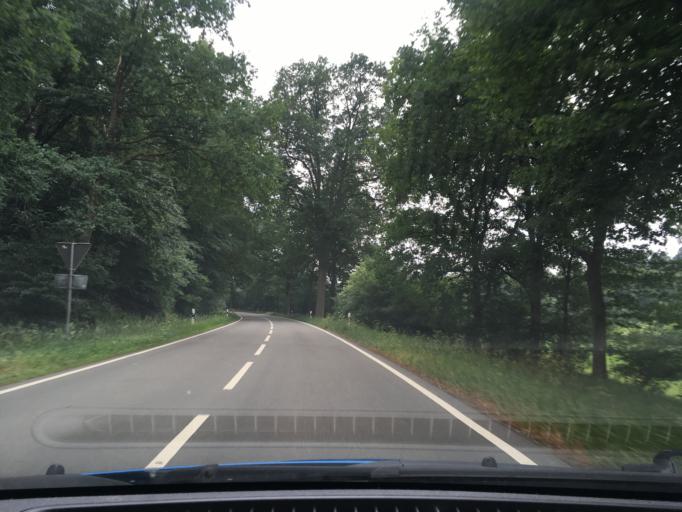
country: DE
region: Lower Saxony
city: Gohrde
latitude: 53.1384
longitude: 10.8775
